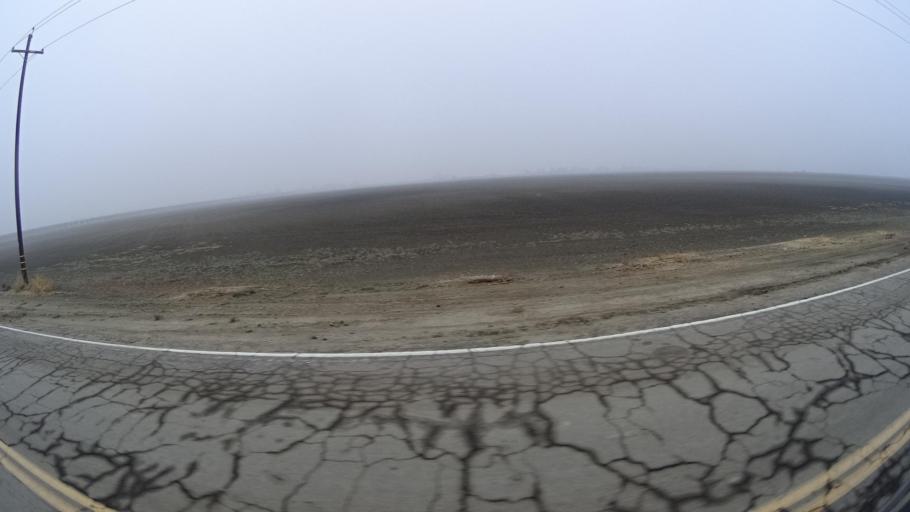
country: US
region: California
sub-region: Kern County
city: Lost Hills
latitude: 35.5378
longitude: -119.6193
